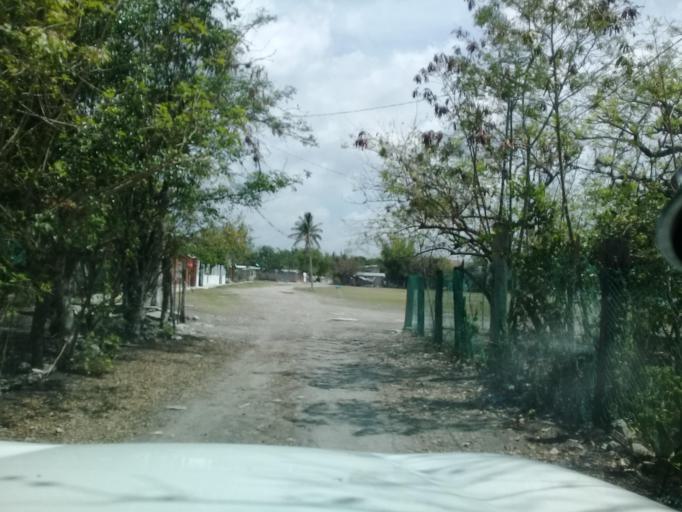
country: MX
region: Veracruz
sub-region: Emiliano Zapata
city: Plan del Rio
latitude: 19.3508
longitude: -96.6458
